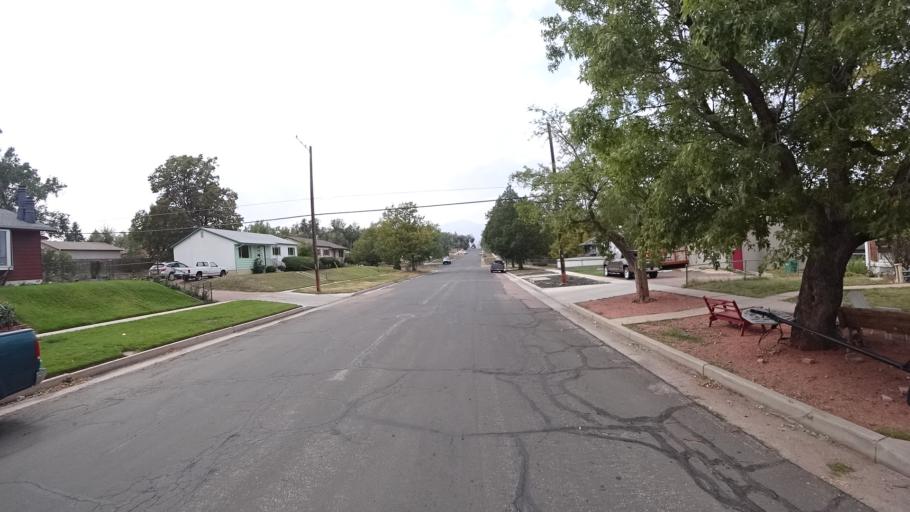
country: US
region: Colorado
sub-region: El Paso County
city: Colorado Springs
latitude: 38.8503
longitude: -104.7835
